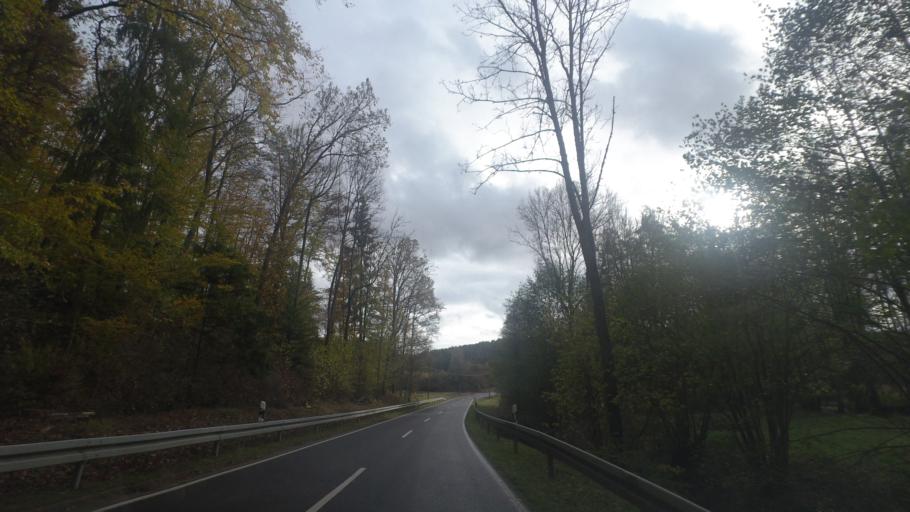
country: DE
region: Bavaria
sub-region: Regierungsbezirk Unterfranken
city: Aubstadt
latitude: 50.3477
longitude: 10.4144
